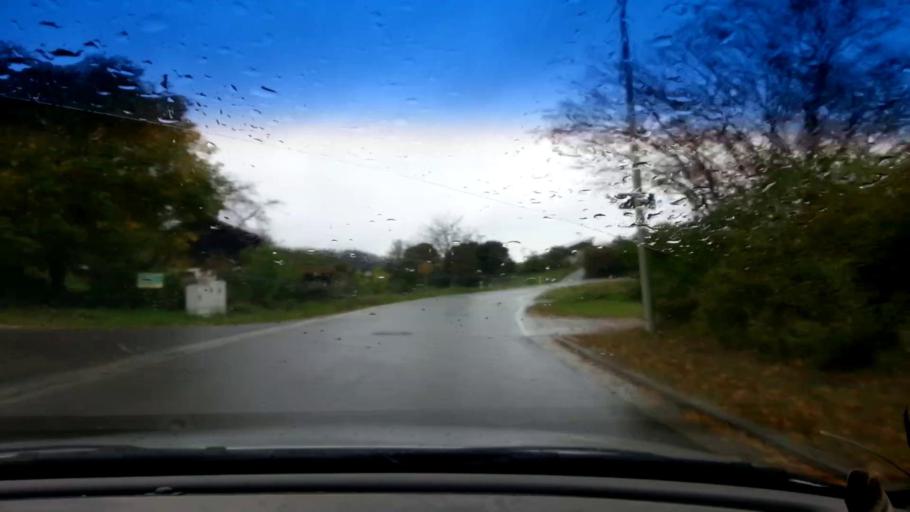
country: DE
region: Bavaria
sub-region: Upper Franconia
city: Poxdorf
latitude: 49.9365
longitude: 11.1194
